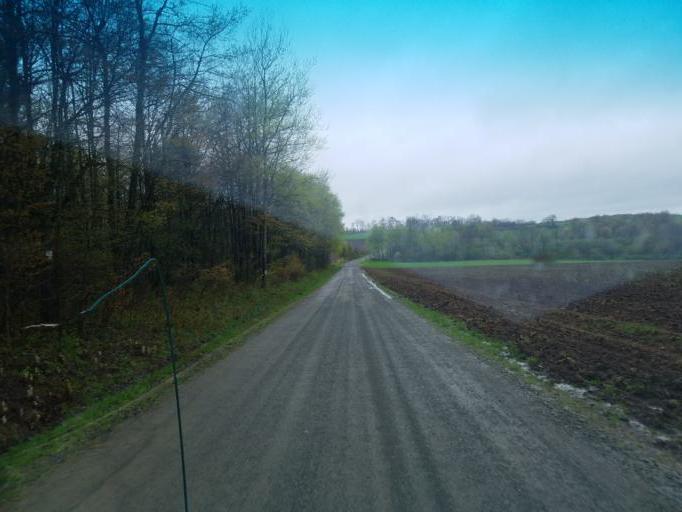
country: US
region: New York
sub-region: Allegany County
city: Andover
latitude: 41.9876
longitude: -77.7187
